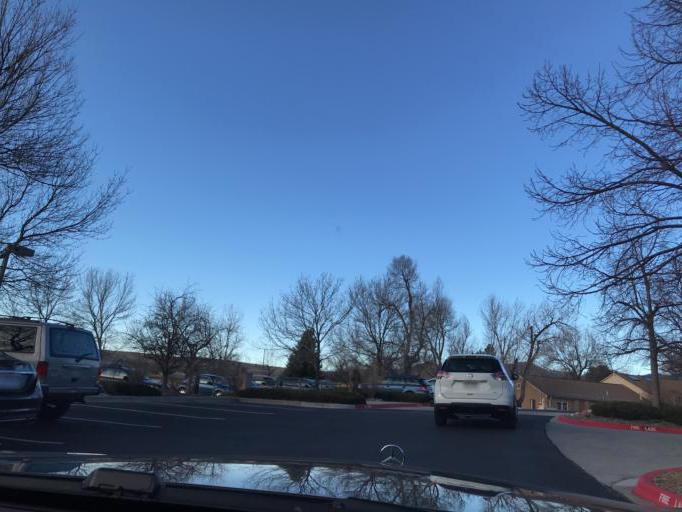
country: US
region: Colorado
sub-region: Boulder County
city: Superior
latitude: 39.9886
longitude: -105.1948
